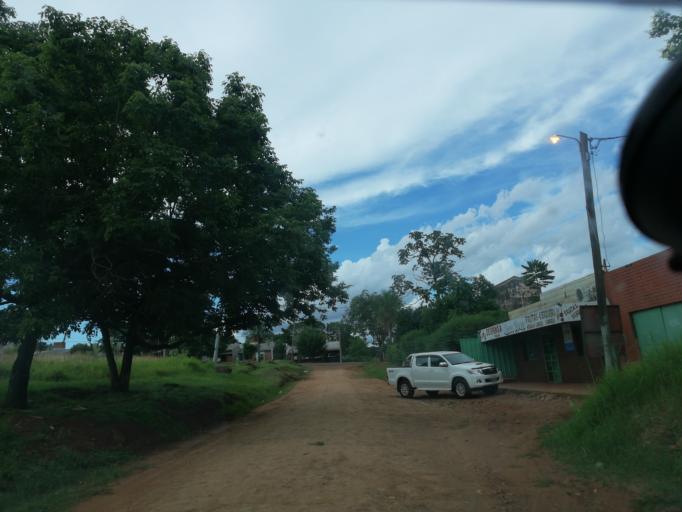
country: AR
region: Misiones
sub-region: Departamento de Capital
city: Posadas
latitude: -27.4205
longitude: -55.9223
